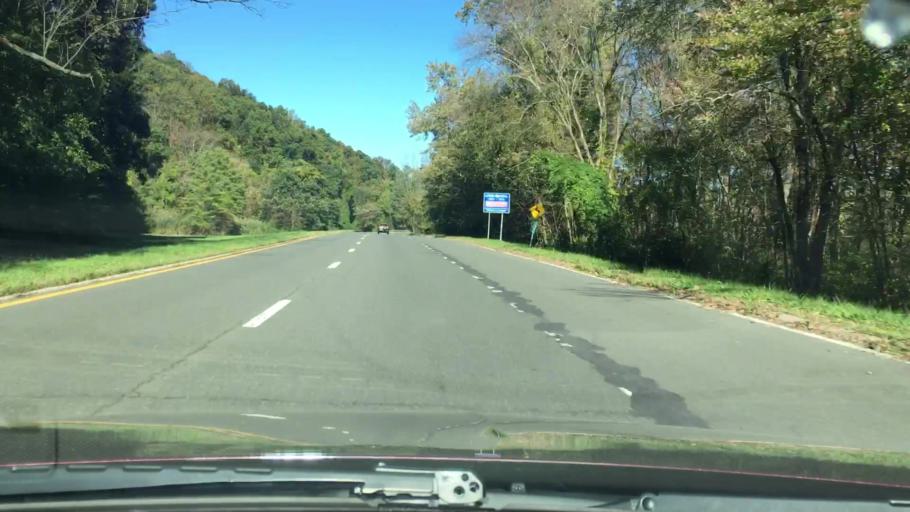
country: US
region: New York
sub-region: Westchester County
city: Bedford Hills
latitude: 41.2283
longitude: -73.7160
